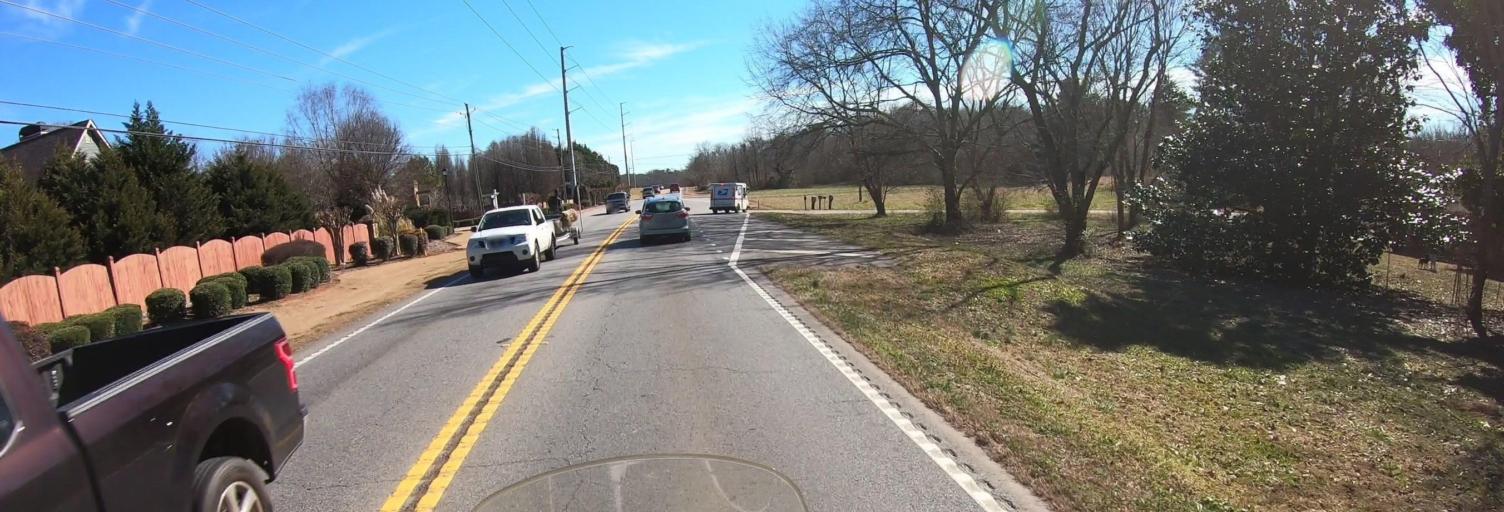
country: US
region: Georgia
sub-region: Forsyth County
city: Cumming
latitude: 34.2789
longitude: -84.1210
